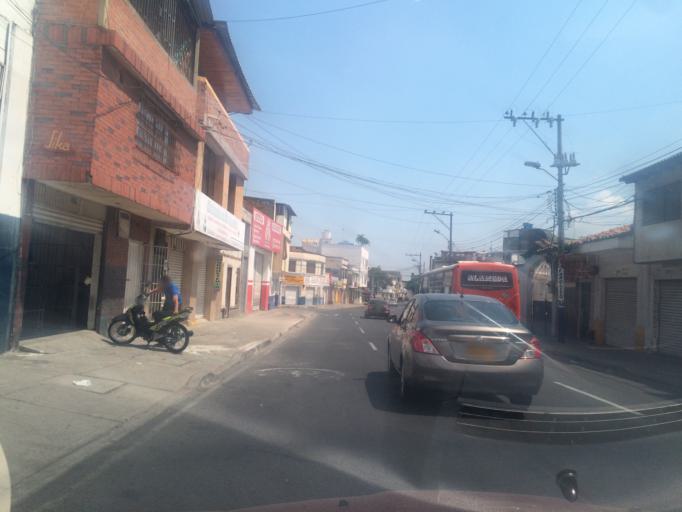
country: CO
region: Valle del Cauca
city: Cali
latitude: 3.4412
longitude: -76.5343
